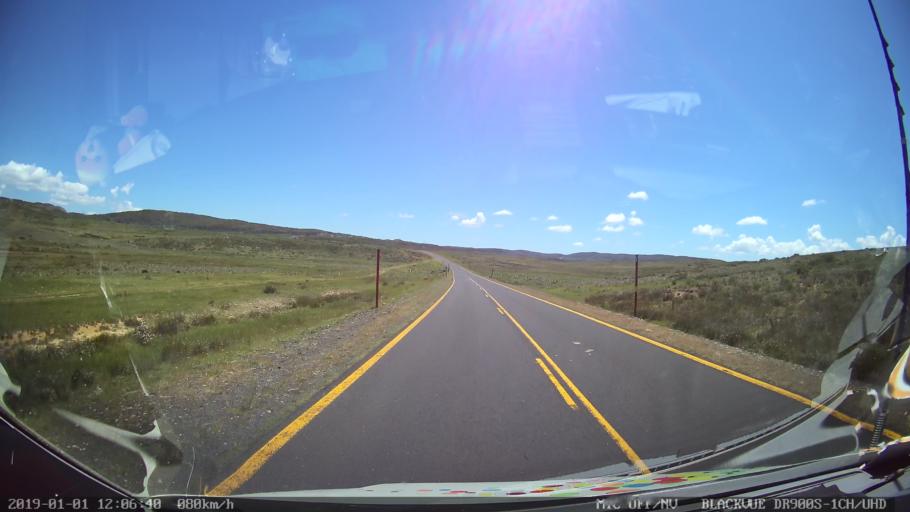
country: AU
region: New South Wales
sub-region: Snowy River
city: Jindabyne
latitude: -35.8422
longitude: 148.4914
